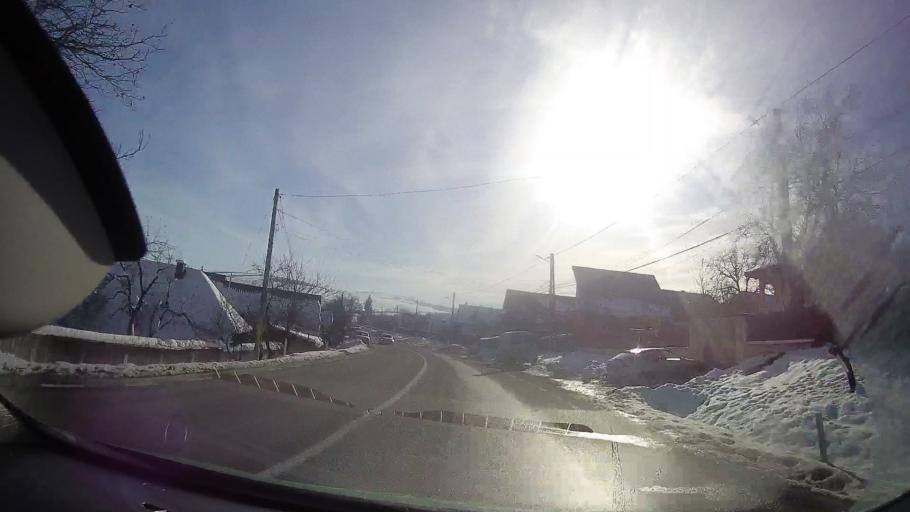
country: RO
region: Neamt
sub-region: Comuna Baltatesti
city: Valea Seaca
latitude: 47.1351
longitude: 26.3139
